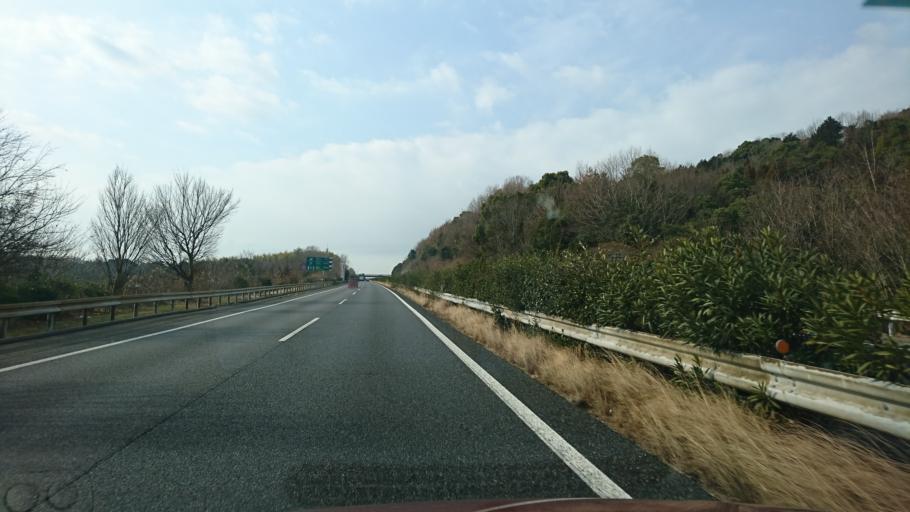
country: JP
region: Okayama
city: Kurashiki
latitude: 34.5776
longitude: 133.6745
